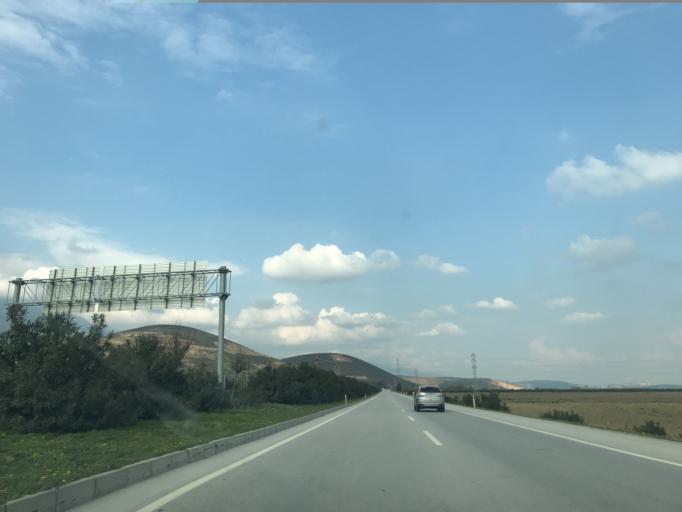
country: TR
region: Hatay
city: Serinyol
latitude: 36.4319
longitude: 36.2795
